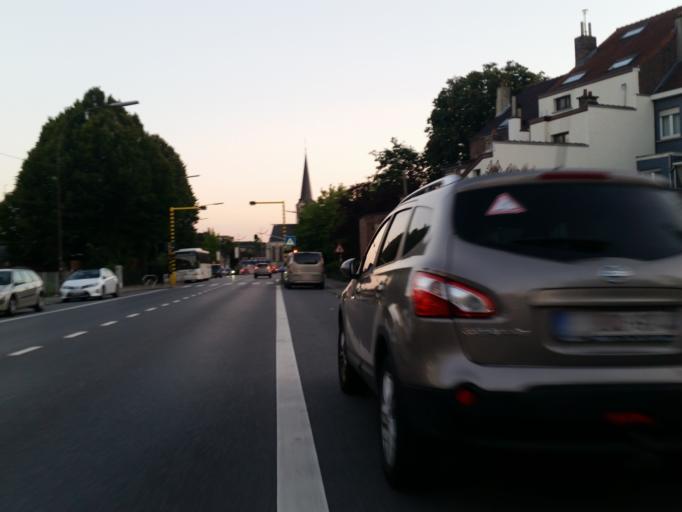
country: BE
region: Flanders
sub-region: Provincie Vlaams-Brabant
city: Zaventem
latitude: 50.8838
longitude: 4.4741
